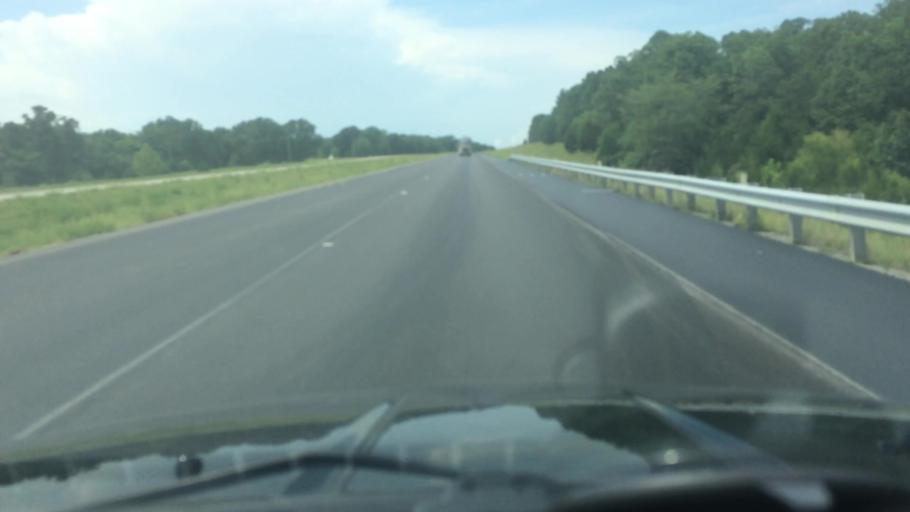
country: US
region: Missouri
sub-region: Saint Clair County
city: Osceola
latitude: 37.9498
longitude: -93.6389
